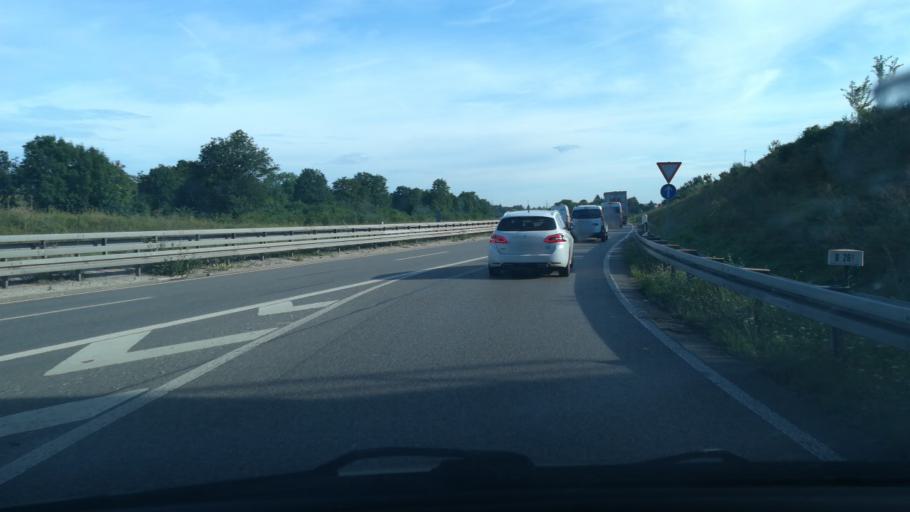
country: DE
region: Baden-Wuerttemberg
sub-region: Tuebingen Region
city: Metzingen
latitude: 48.5290
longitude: 9.2631
